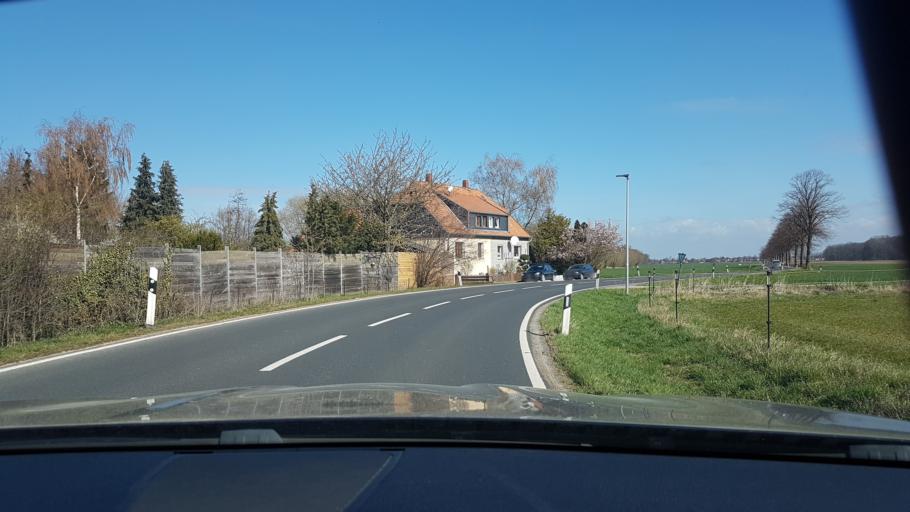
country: DE
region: Lower Saxony
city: Pattensen
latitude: 52.2211
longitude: 9.7113
